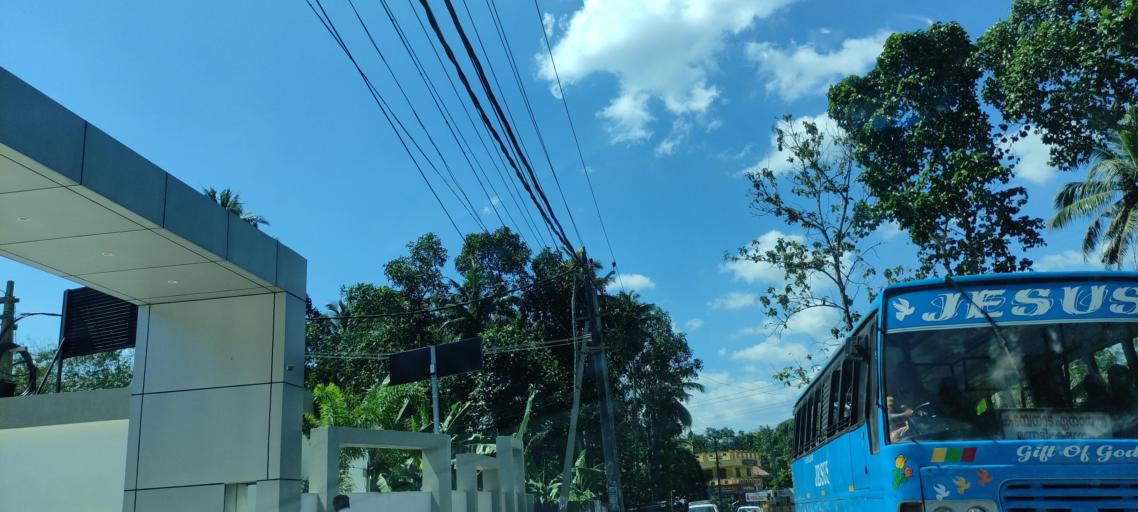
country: IN
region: Kerala
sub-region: Pattanamtitta
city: Adur
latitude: 9.0906
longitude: 76.6911
